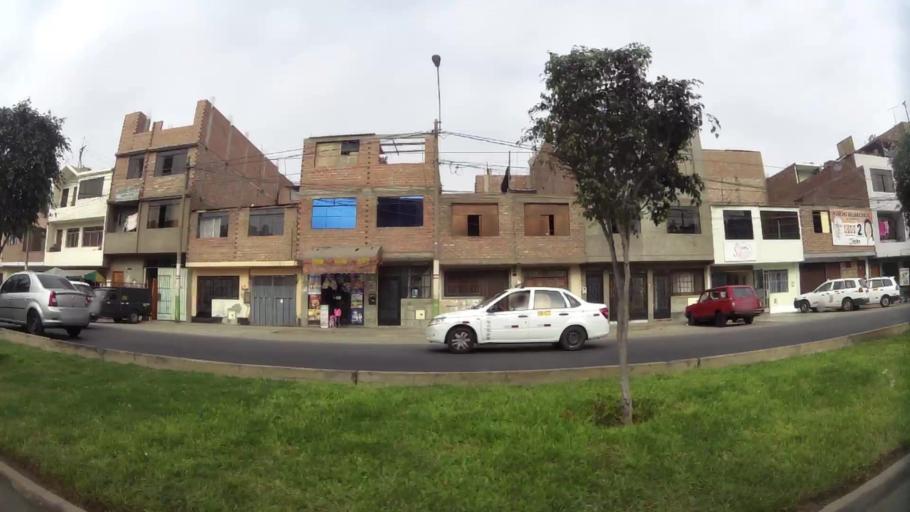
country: PE
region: Callao
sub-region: Callao
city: Callao
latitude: -12.0262
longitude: -77.0995
